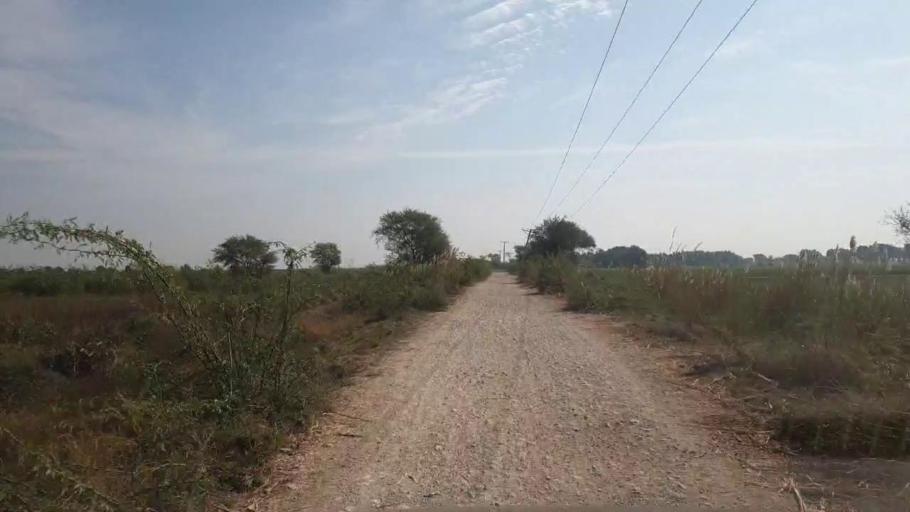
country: PK
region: Sindh
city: Mirwah Gorchani
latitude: 25.3748
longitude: 69.1978
